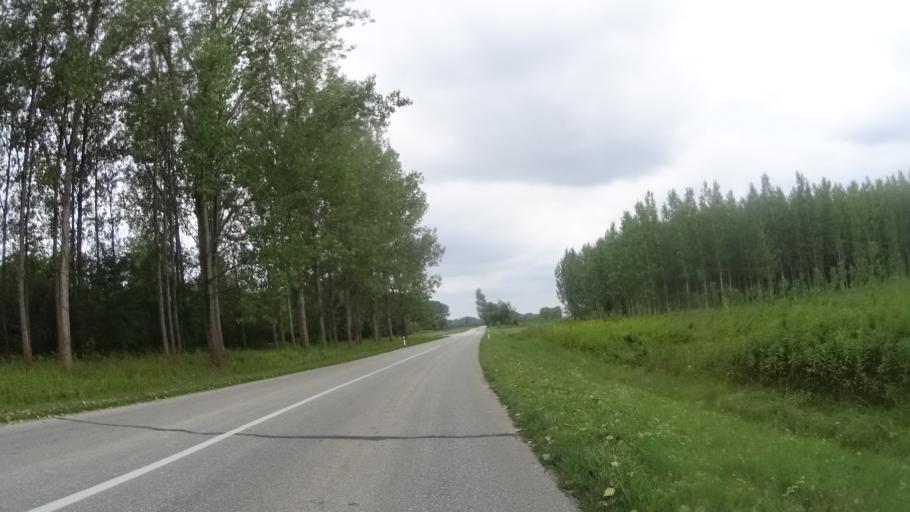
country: HU
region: Gyor-Moson-Sopron
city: Bony
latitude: 47.7488
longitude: 17.8742
